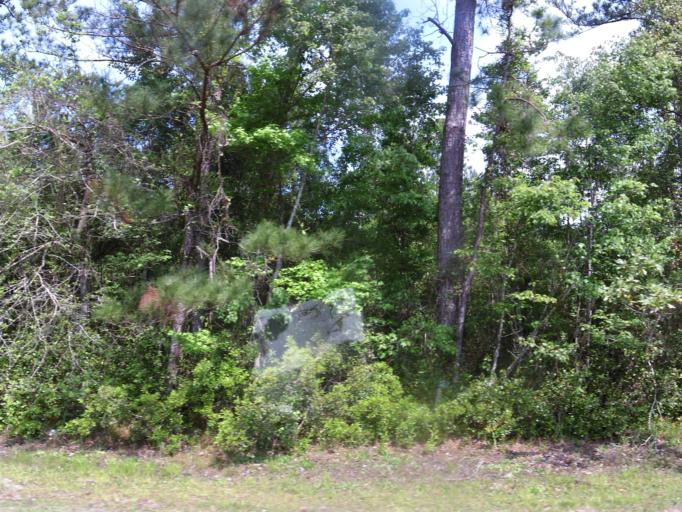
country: US
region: Georgia
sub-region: Camden County
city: Kingsland
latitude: 30.8097
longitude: -81.7513
